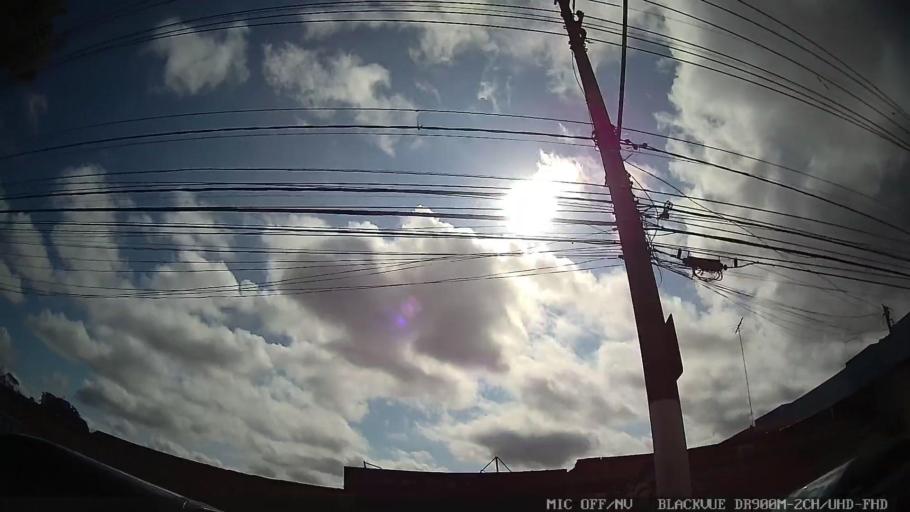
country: BR
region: Sao Paulo
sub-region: Guarulhos
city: Guarulhos
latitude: -23.5288
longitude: -46.4742
